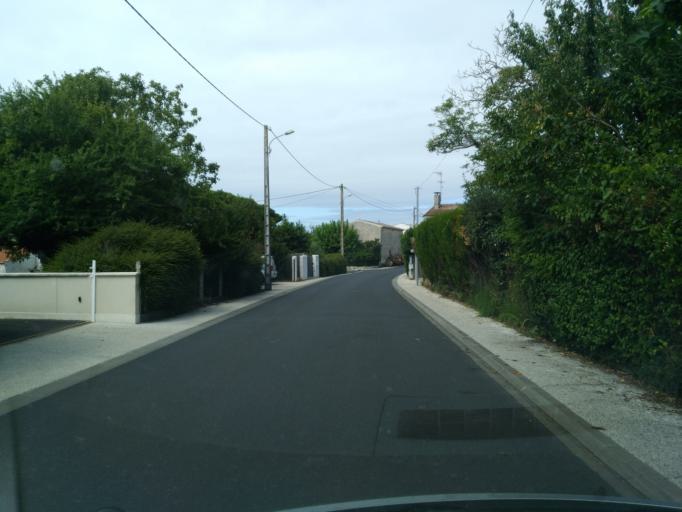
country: FR
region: Poitou-Charentes
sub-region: Departement de la Charente-Maritime
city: Saint-Palais-sur-Mer
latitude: 45.6537
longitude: -1.0808
